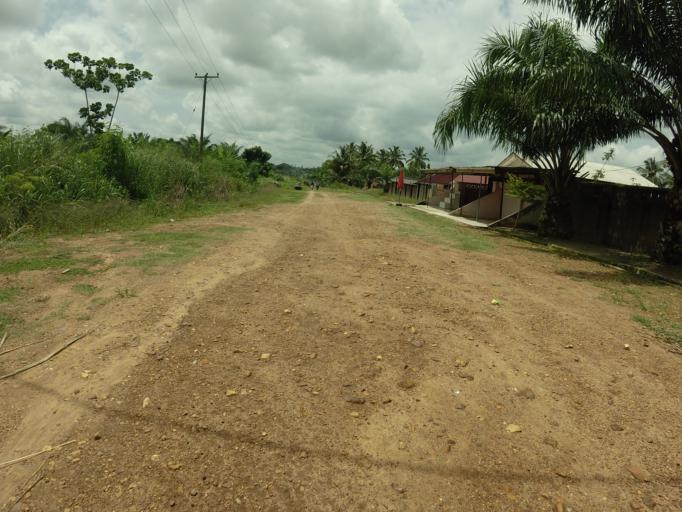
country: GH
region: Volta
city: Ho
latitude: 6.5955
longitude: 0.4818
